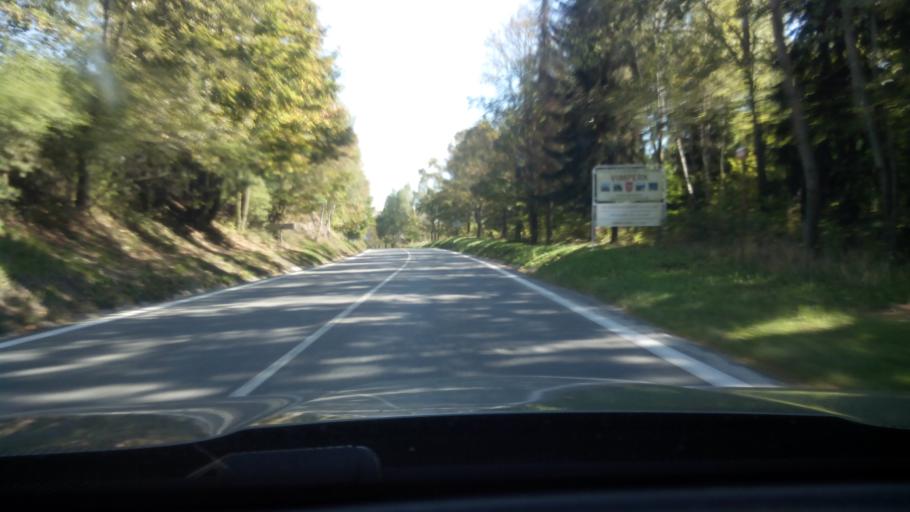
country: CZ
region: Jihocesky
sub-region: Okres Prachatice
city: Vimperk
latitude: 49.0615
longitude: 13.7569
